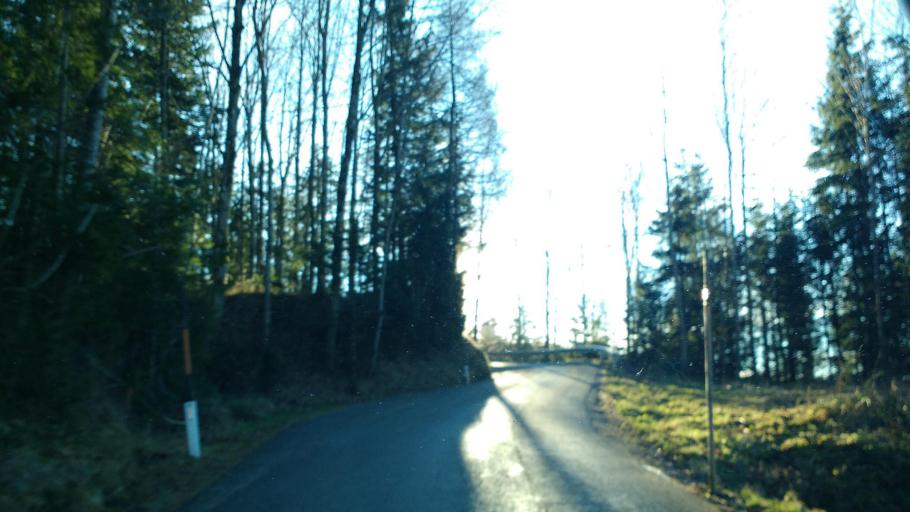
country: AT
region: Upper Austria
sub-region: Politischer Bezirk Kirchdorf an der Krems
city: Micheldorf in Oberoesterreich
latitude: 47.9073
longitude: 14.1483
